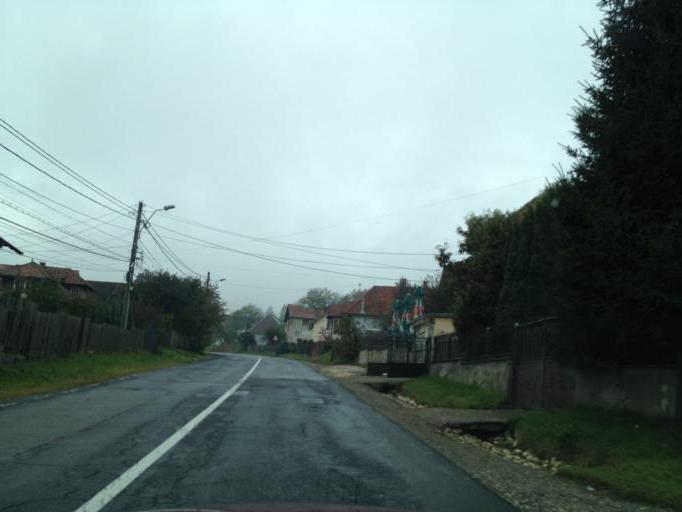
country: RO
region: Brasov
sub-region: Comuna Moeciu
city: Moieciu de Jos
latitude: 45.4970
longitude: 25.3274
